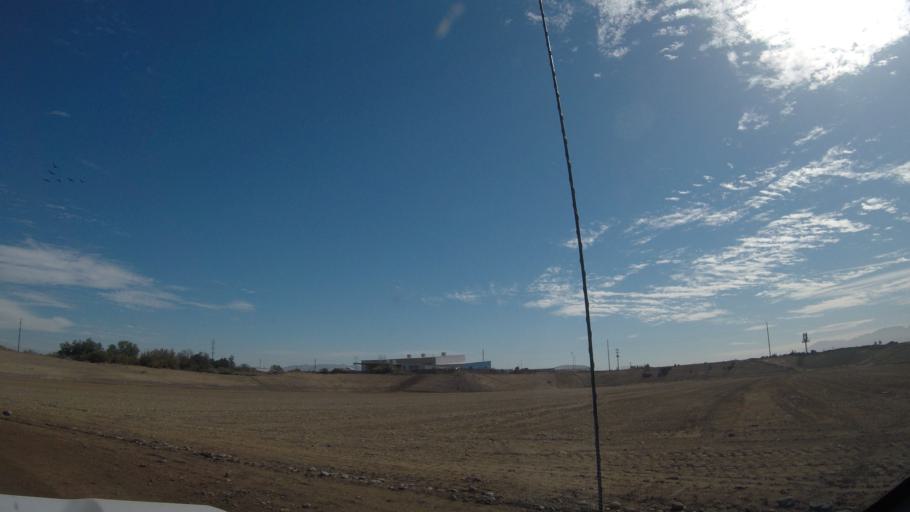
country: US
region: Arizona
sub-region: Maricopa County
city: Laveen
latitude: 33.3945
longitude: -112.1908
